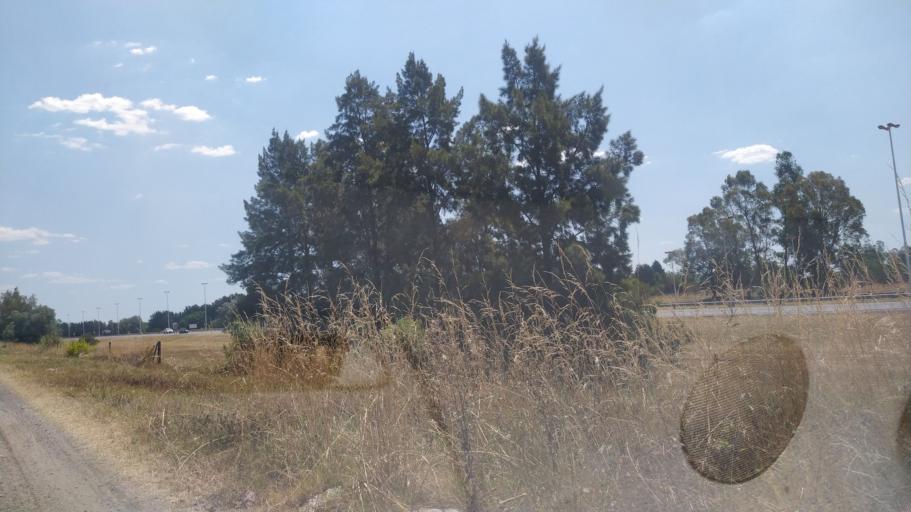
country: AR
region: Buenos Aires
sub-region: Partido de Ezeiza
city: Ezeiza
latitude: -34.9074
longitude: -58.6233
